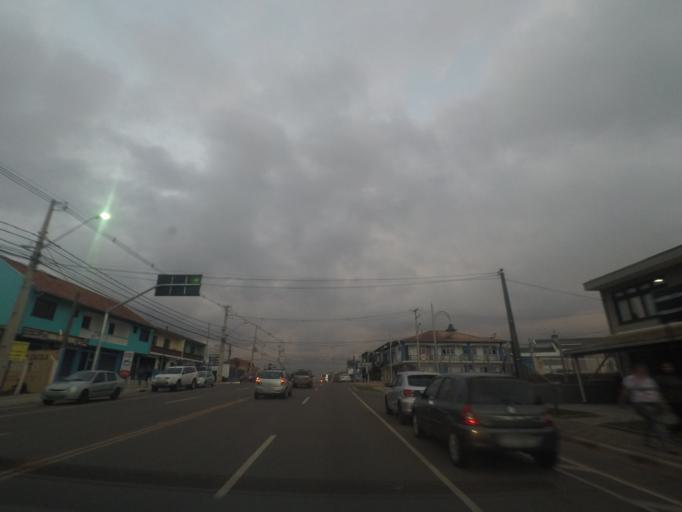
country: BR
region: Parana
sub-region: Curitiba
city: Curitiba
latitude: -25.3961
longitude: -49.3461
